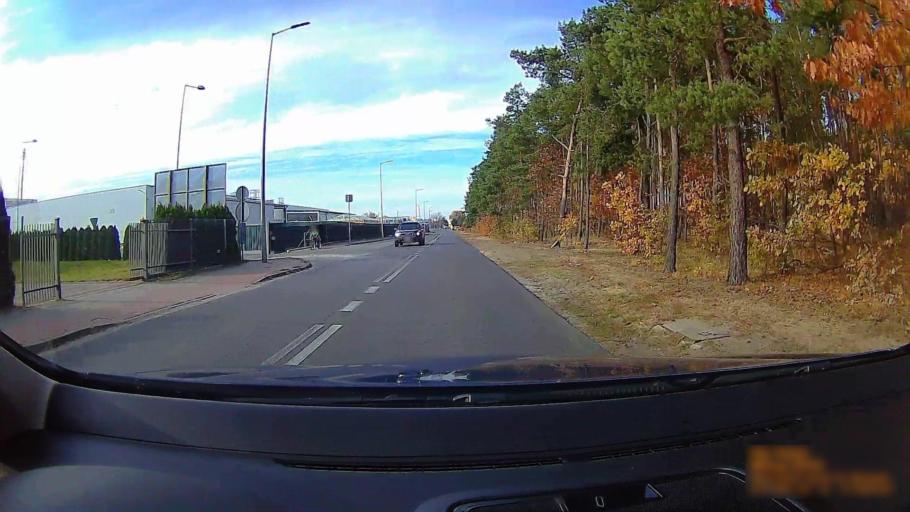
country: PL
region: Greater Poland Voivodeship
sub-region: Powiat ostrzeszowski
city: Ostrzeszow
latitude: 51.4354
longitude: 17.9187
